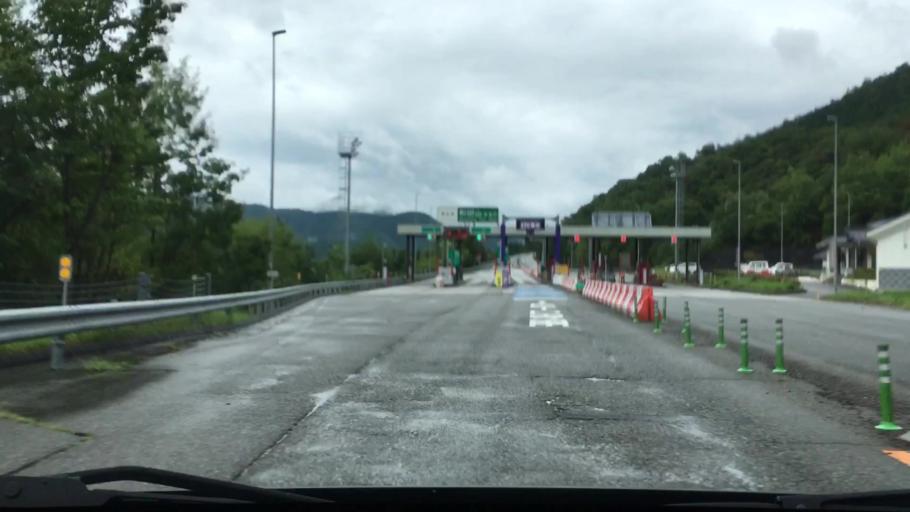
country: JP
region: Hyogo
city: Toyooka
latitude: 35.2871
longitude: 134.8225
